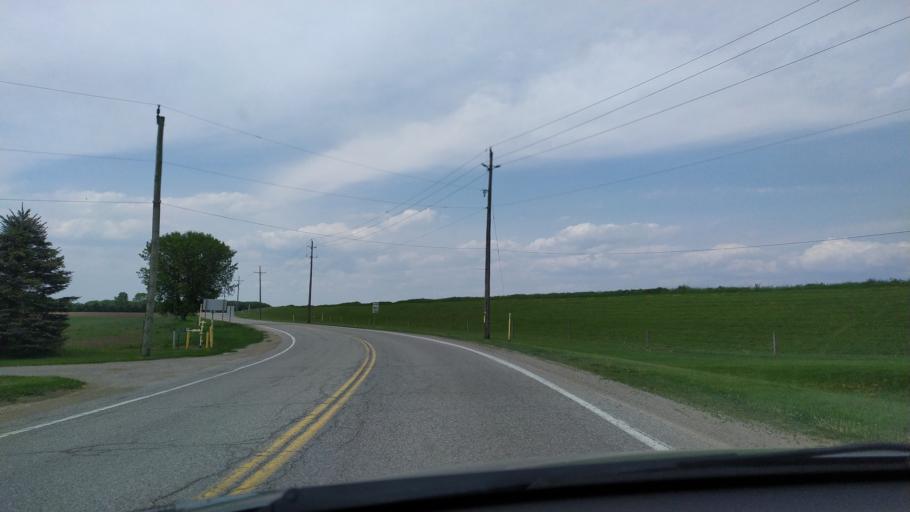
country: CA
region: Ontario
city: Ingersoll
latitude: 42.9923
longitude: -80.9552
